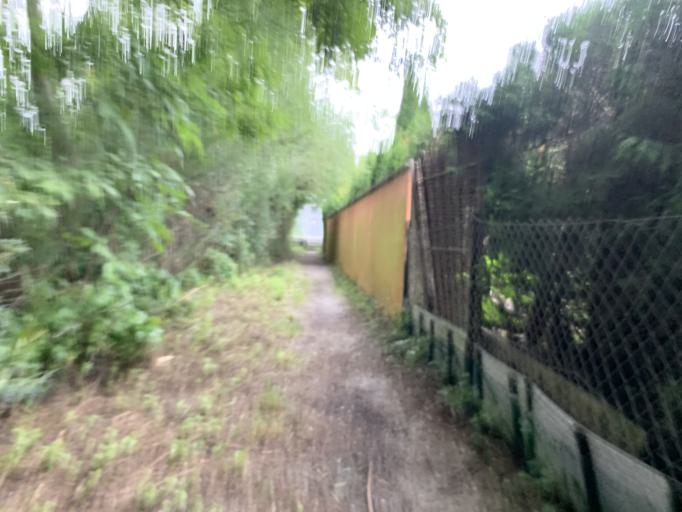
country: DE
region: Bavaria
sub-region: Upper Bavaria
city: Freising
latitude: 48.3917
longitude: 11.7328
